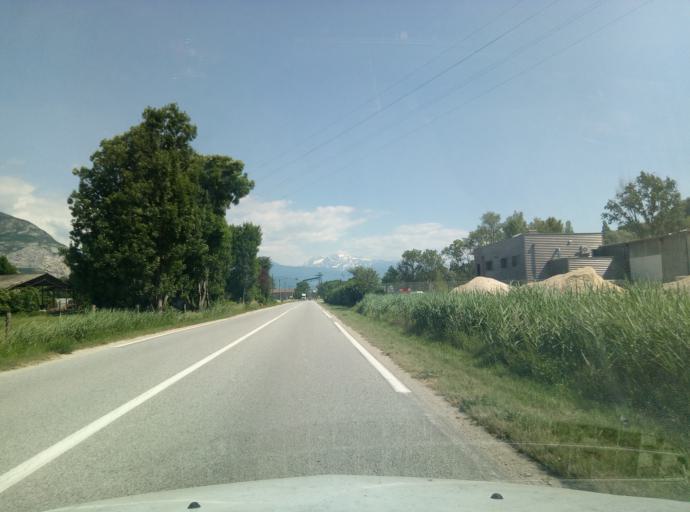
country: FR
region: Rhone-Alpes
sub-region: Departement de l'Isere
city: Fontanil-Cornillon
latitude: 45.2269
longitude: 5.6535
